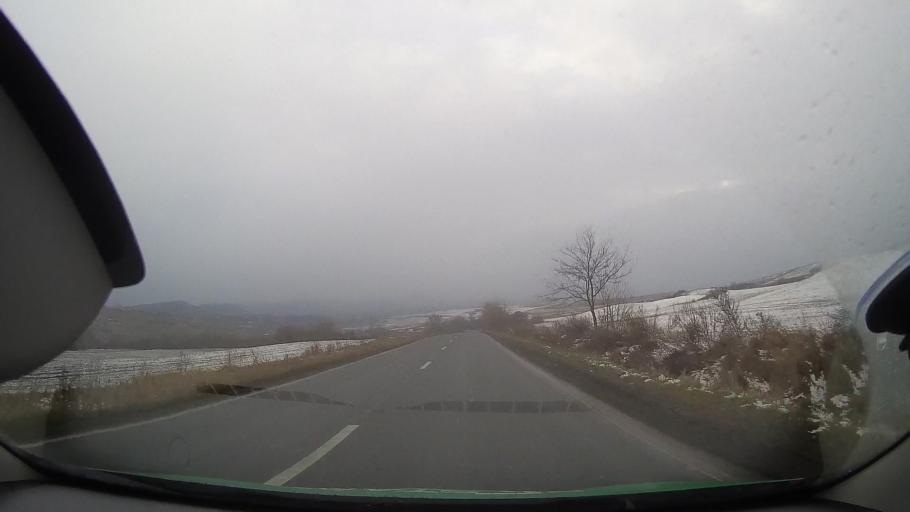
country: RO
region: Sibiu
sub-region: Comuna Blajel
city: Blajel
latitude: 46.2486
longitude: 24.3000
